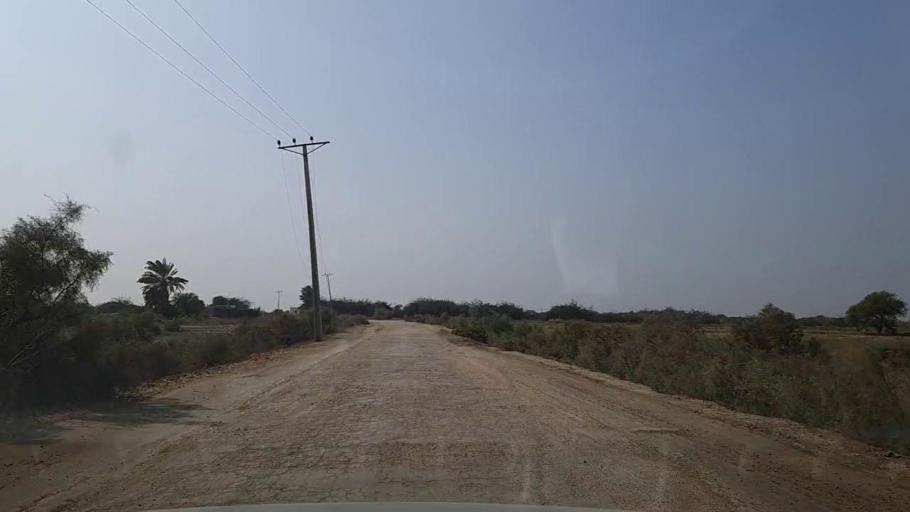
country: PK
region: Sindh
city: Mirpur Sakro
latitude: 24.5454
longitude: 67.6096
